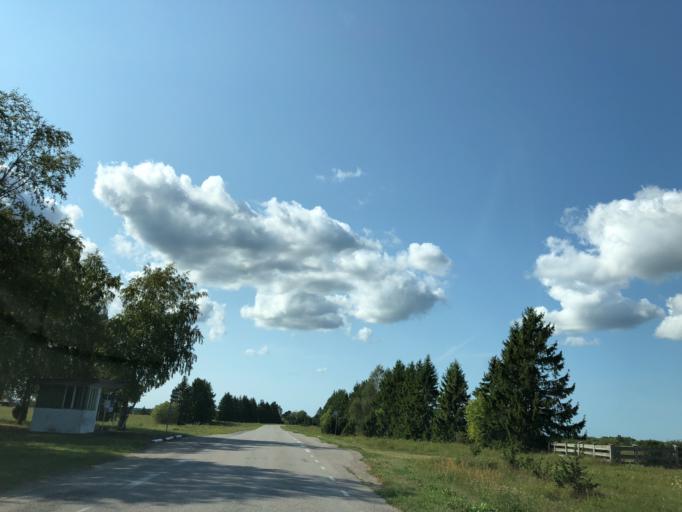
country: EE
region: Hiiumaa
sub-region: Kaerdla linn
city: Kardla
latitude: 58.7854
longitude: 22.7841
